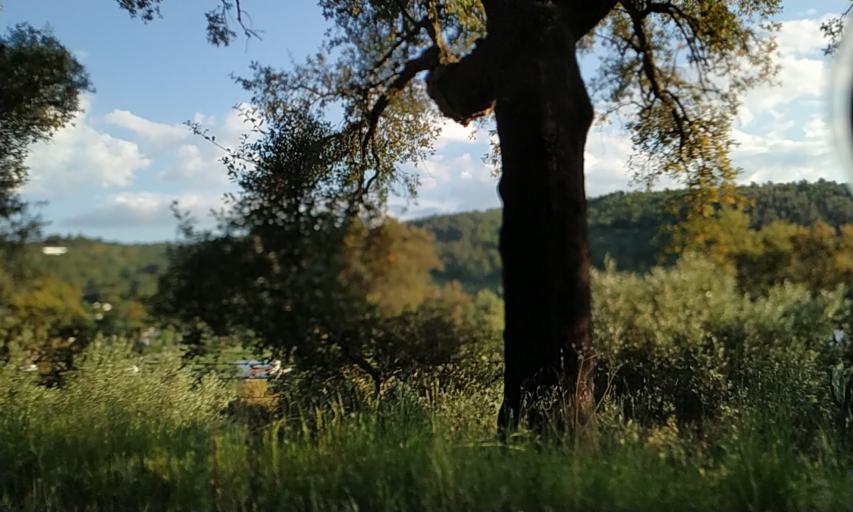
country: PT
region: Portalegre
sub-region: Portalegre
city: Portalegre
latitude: 39.3260
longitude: -7.4225
